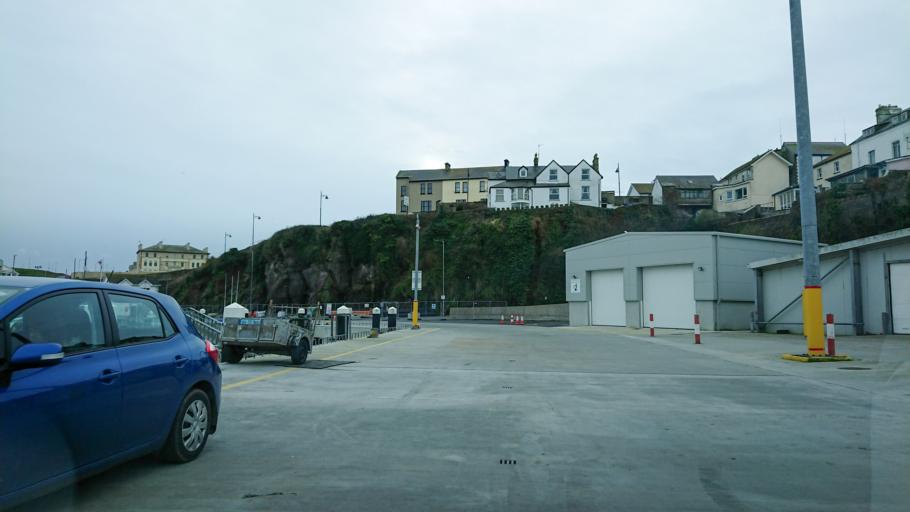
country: IE
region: Munster
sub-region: Waterford
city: Dunmore East
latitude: 52.1484
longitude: -6.9918
